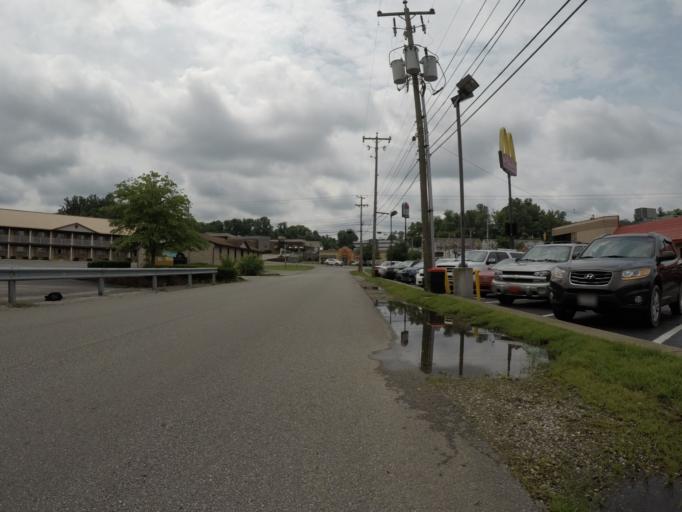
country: US
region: West Virginia
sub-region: Cabell County
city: Pea Ridge
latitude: 38.4137
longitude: -82.3436
